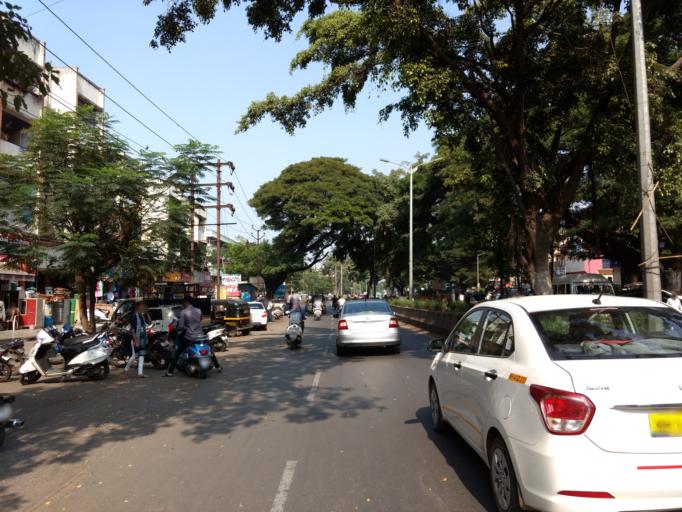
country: IN
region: Maharashtra
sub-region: Pune Division
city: Pune
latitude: 18.4775
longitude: 73.8620
